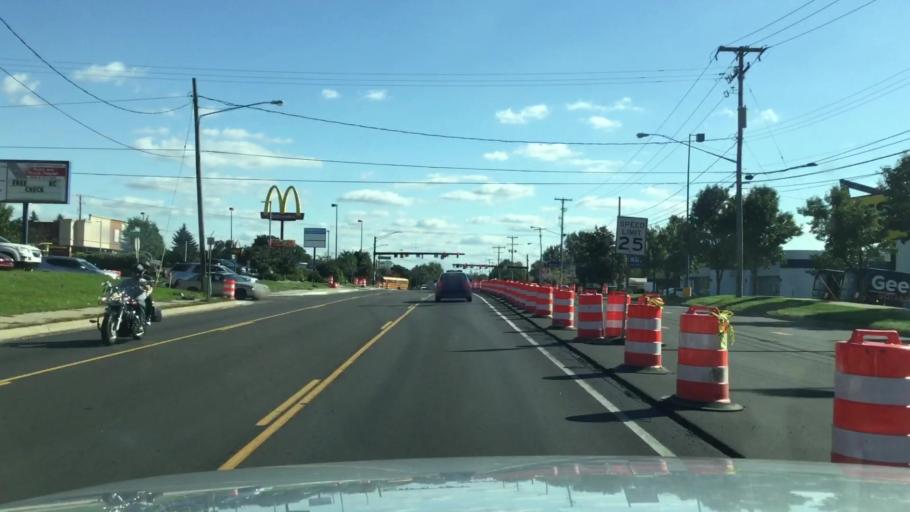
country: US
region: Michigan
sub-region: Kalamazoo County
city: Portage
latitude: 42.2173
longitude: -85.5894
